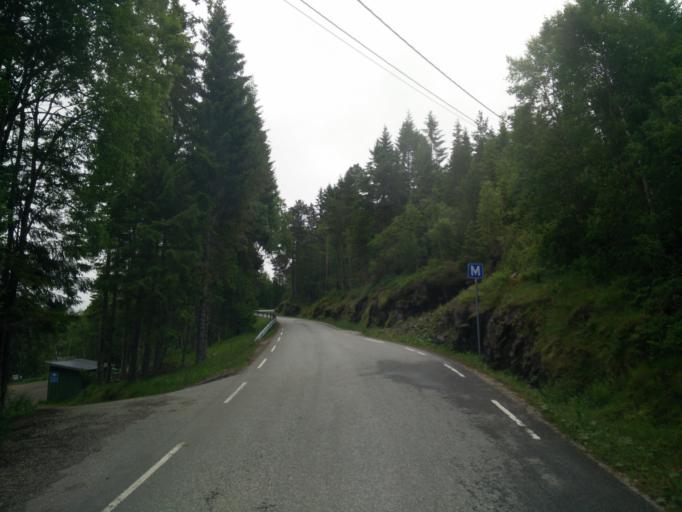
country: NO
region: More og Romsdal
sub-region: Kristiansund
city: Rensvik
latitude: 63.0191
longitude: 7.9572
